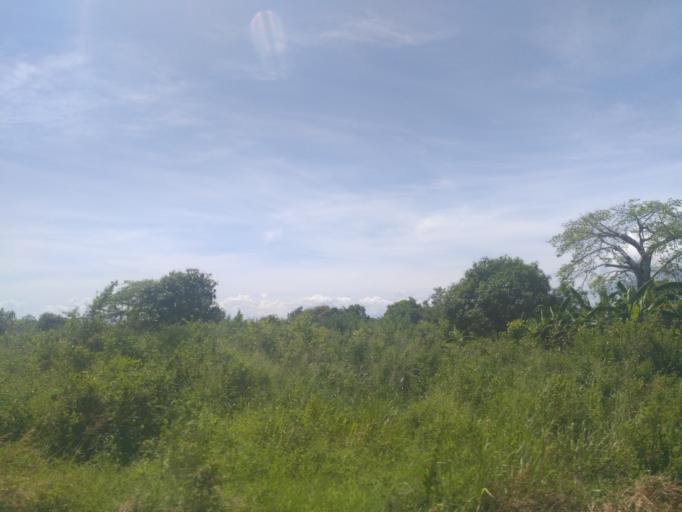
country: TZ
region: Zanzibar North
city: Gamba
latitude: -5.9264
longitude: 39.3478
